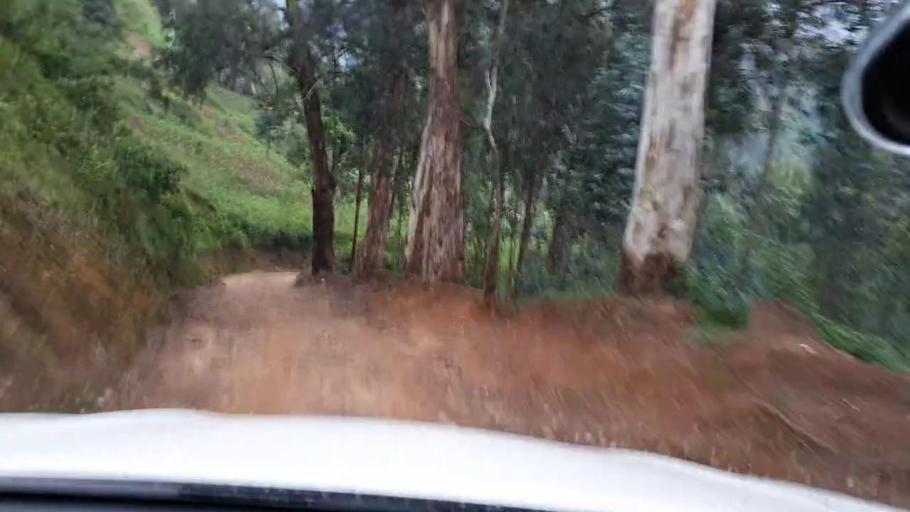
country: RW
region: Western Province
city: Cyangugu
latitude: -2.3975
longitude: 29.2305
